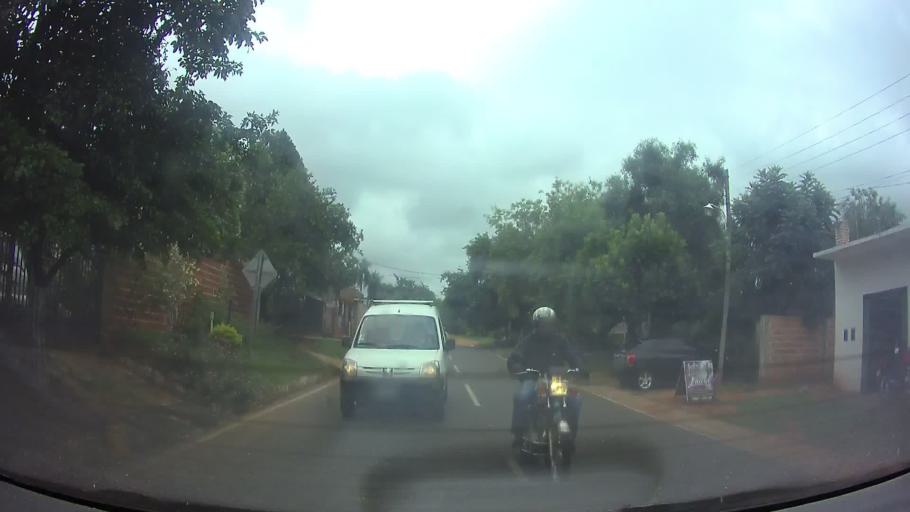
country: PY
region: Paraguari
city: Carapegua
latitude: -25.7621
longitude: -57.2512
